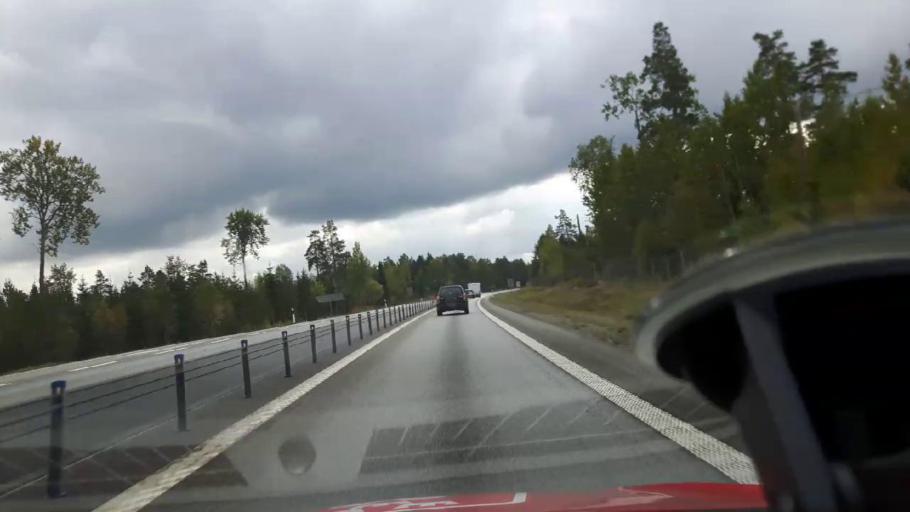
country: SE
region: Gaevleborg
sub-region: Gavle Kommun
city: Gavle
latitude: 60.7932
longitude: 17.0825
